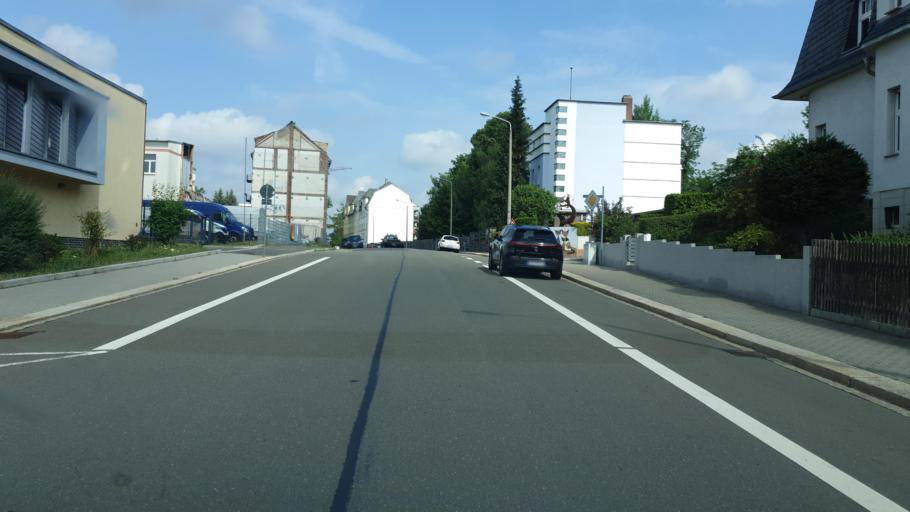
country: DE
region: Saxony
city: Reichenbach/Vogtland
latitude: 50.6288
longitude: 12.3030
